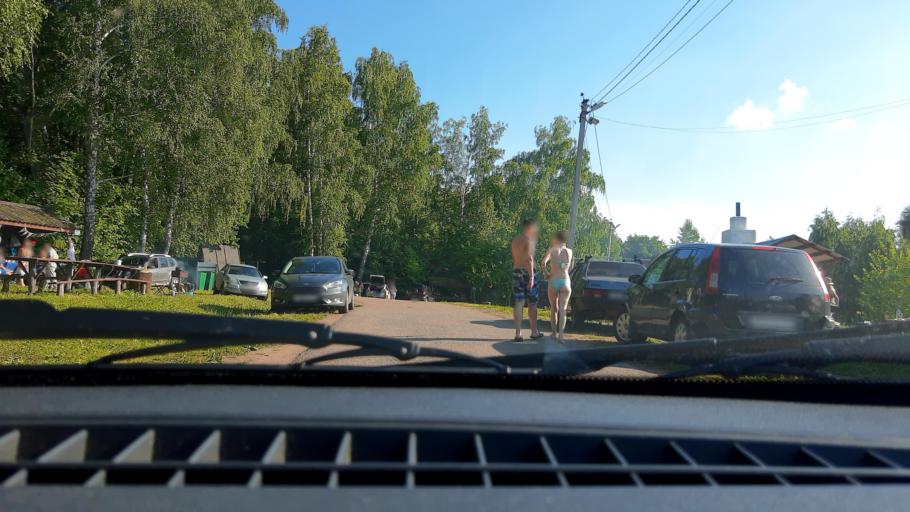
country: RU
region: Bashkortostan
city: Mikhaylovka
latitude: 54.8310
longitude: 55.8589
